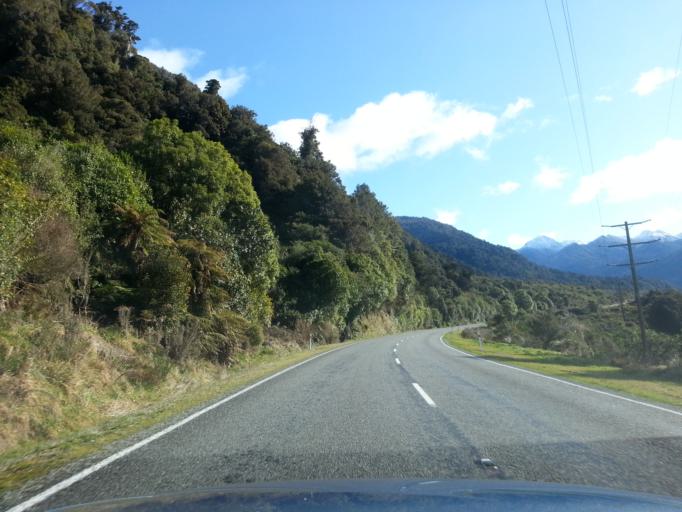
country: NZ
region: West Coast
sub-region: Grey District
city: Greymouth
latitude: -42.7442
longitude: 171.4782
